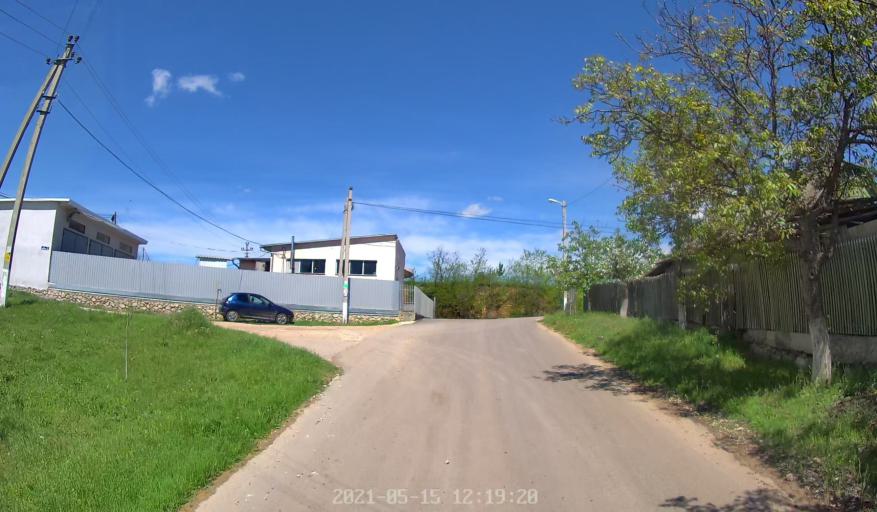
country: MD
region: Hincesti
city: Hincesti
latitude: 46.8010
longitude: 28.5403
